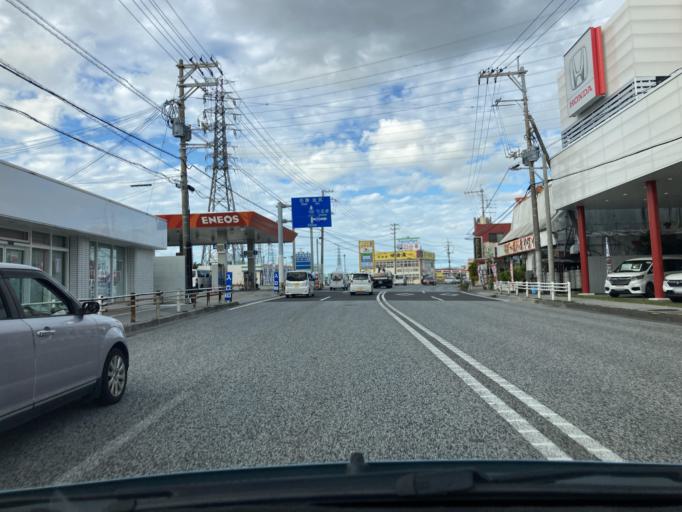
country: JP
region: Okinawa
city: Ishikawa
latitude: 26.3852
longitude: 127.8276
